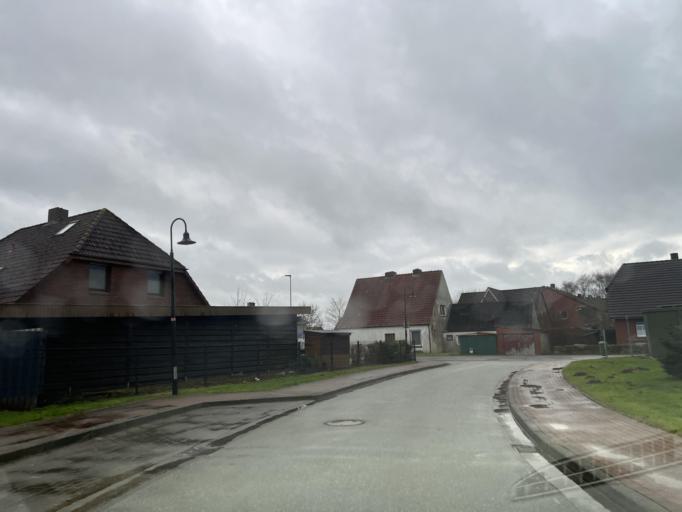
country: DE
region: Schleswig-Holstein
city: Neuenkirchen
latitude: 54.2372
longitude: 8.9875
